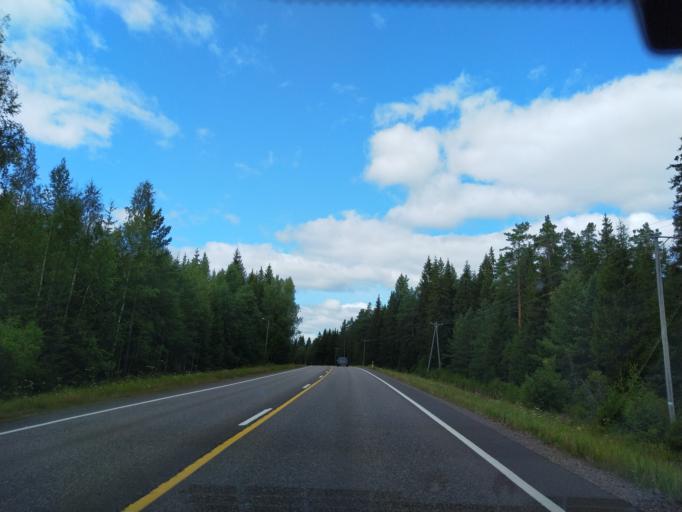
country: FI
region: Haeme
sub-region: Haemeenlinna
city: Renko
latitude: 60.7585
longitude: 24.2944
